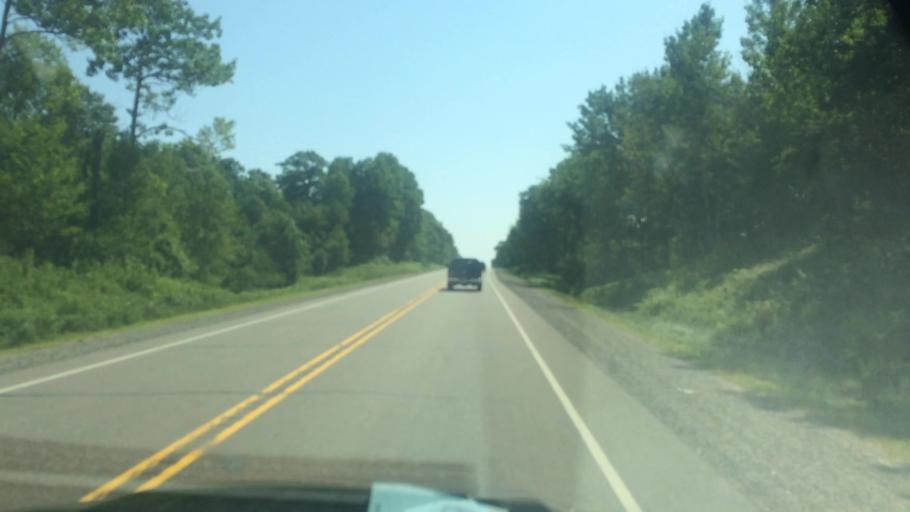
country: US
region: Wisconsin
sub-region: Lincoln County
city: Tomahawk
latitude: 45.5706
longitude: -89.6052
